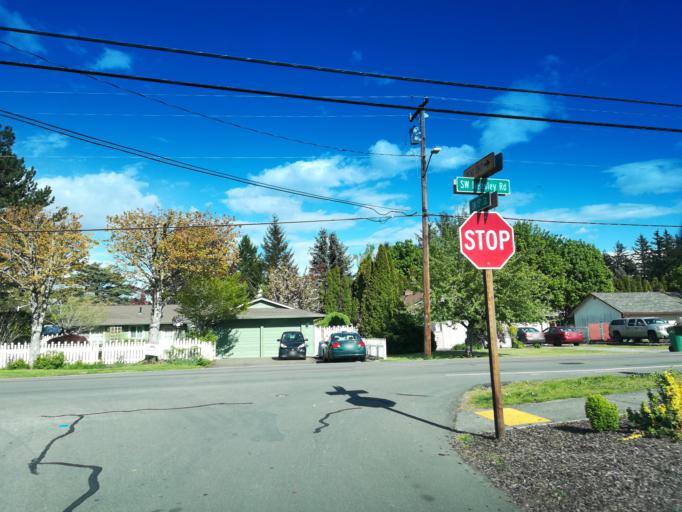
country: US
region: Oregon
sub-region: Multnomah County
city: Troutdale
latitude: 45.5302
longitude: -122.3936
